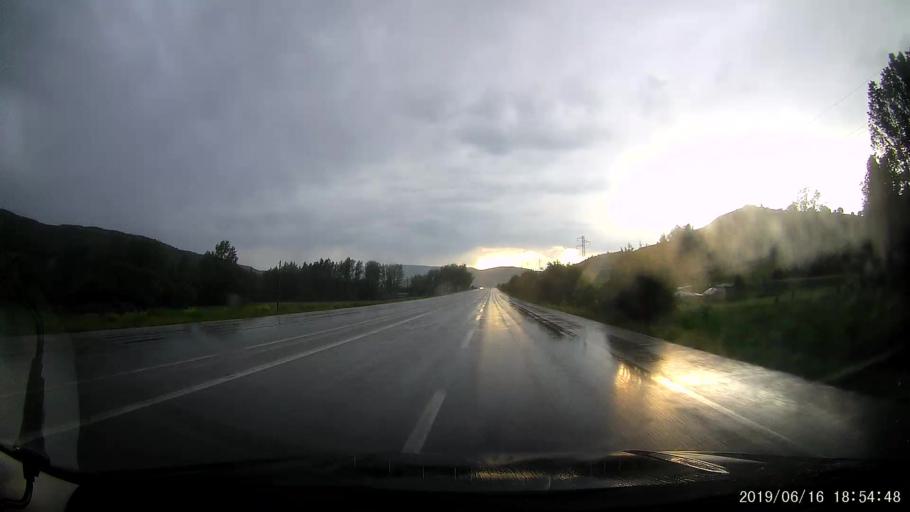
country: TR
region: Erzincan
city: Catalcam
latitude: 39.8980
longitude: 38.8443
